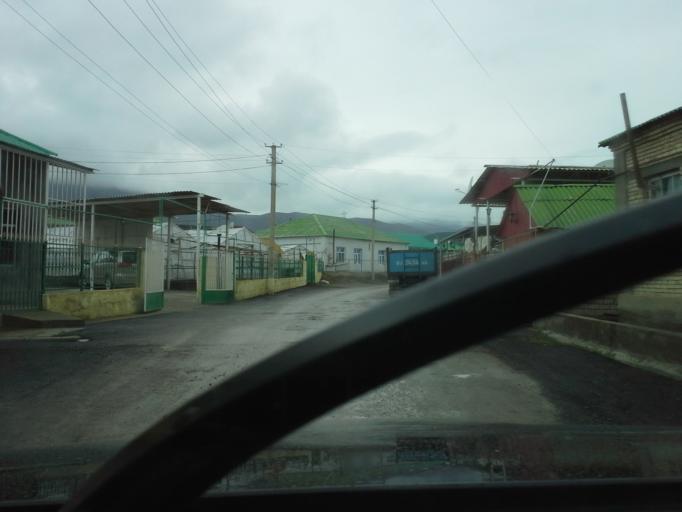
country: TM
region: Ahal
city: Abadan
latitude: 37.9614
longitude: 58.2064
